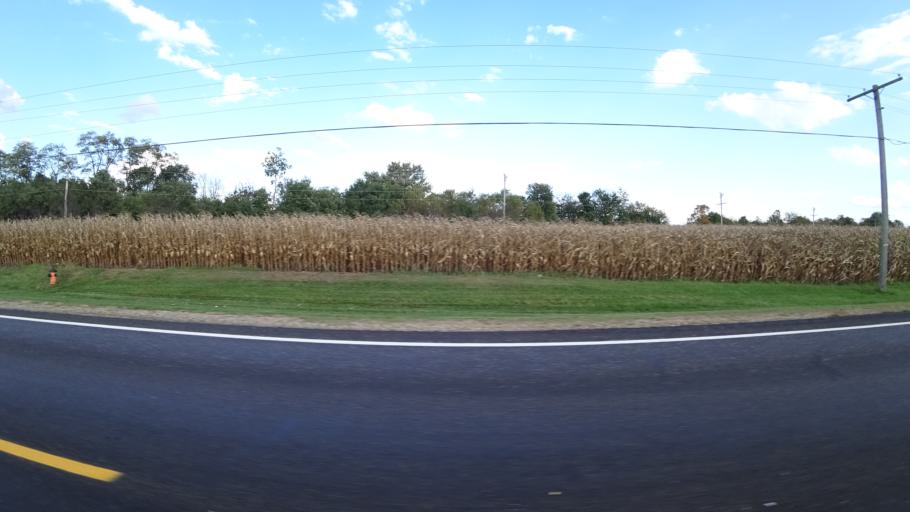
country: US
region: Michigan
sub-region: Saint Joseph County
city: Sturgis
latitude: 41.8213
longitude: -85.4285
